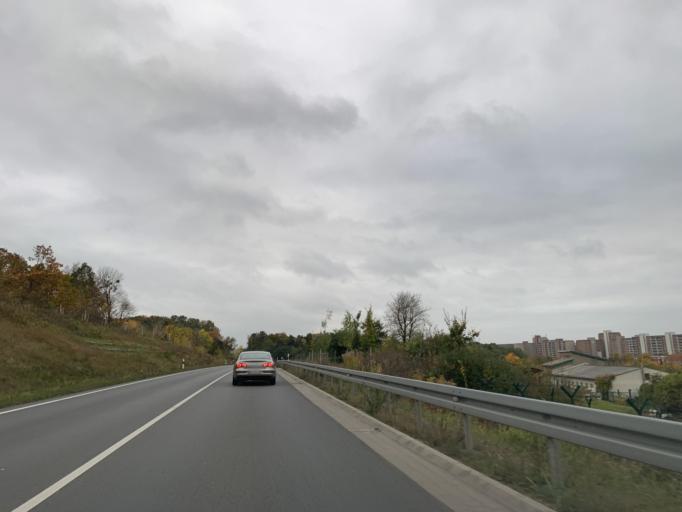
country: DE
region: Mecklenburg-Vorpommern
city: Neubrandenburg
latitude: 53.5473
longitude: 13.2750
